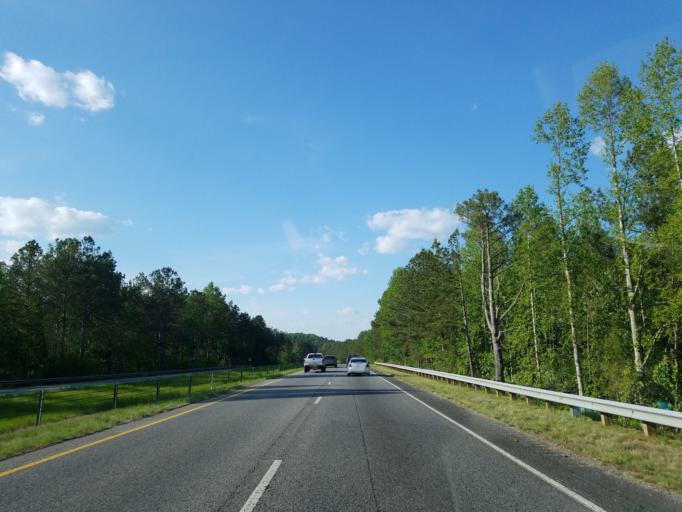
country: US
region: Georgia
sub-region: Lumpkin County
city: Dahlonega
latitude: 34.4196
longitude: -83.9916
